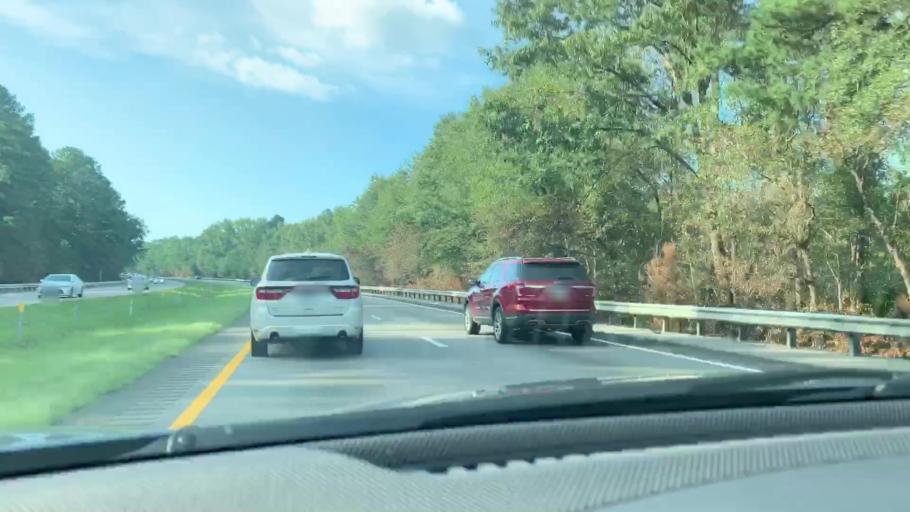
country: US
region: South Carolina
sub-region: Calhoun County
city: Oak Grove
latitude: 33.7542
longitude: -80.9460
